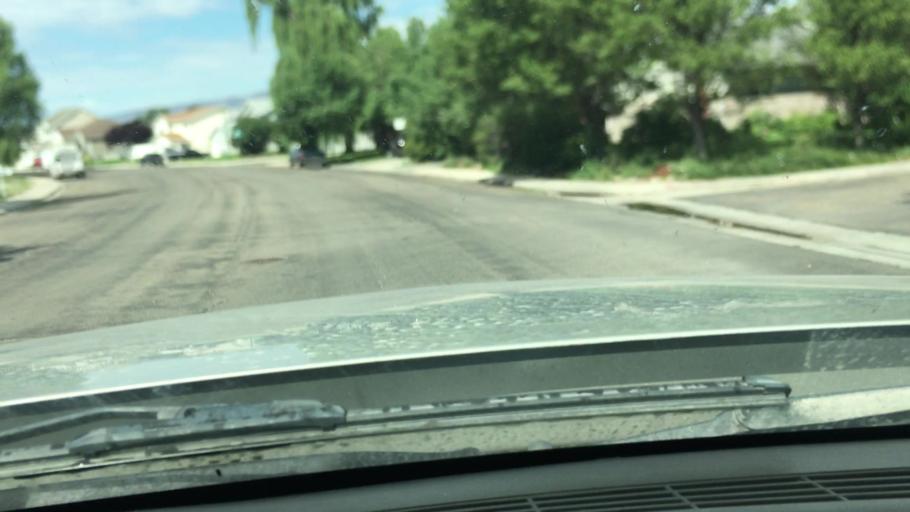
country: US
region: Utah
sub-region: Utah County
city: Orem
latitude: 40.2822
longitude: -111.7356
